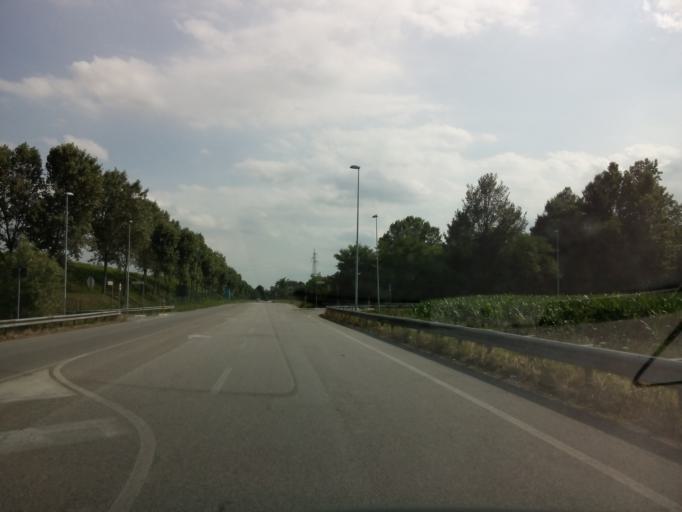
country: IT
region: Veneto
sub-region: Provincia di Padova
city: Limena
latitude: 45.4561
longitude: 11.8356
